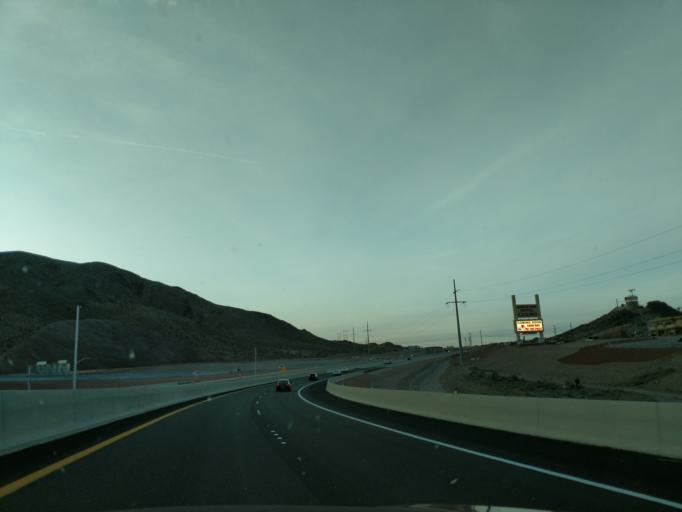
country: US
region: Nevada
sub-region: Clark County
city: Boulder City
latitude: 35.9695
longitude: -114.9123
